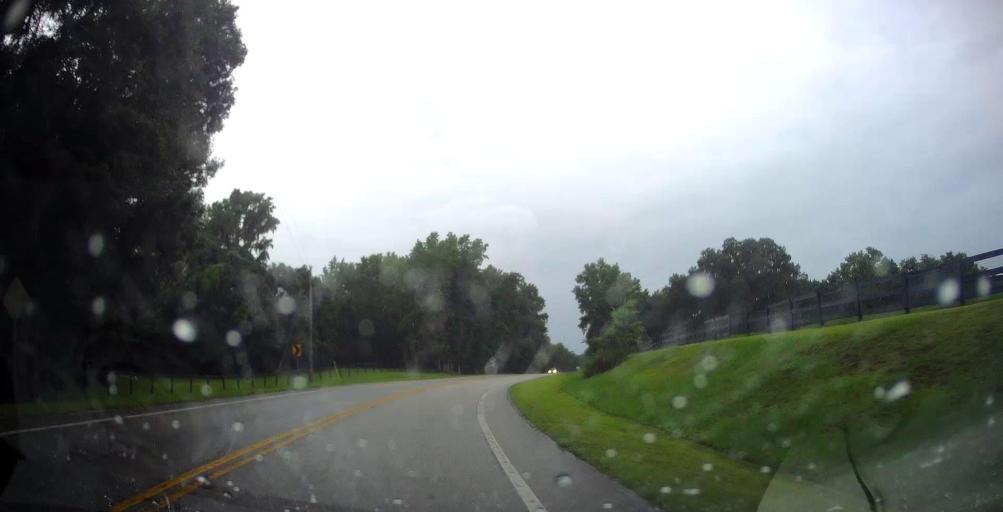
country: US
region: Florida
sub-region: Marion County
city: Citra
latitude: 29.3897
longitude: -82.2478
